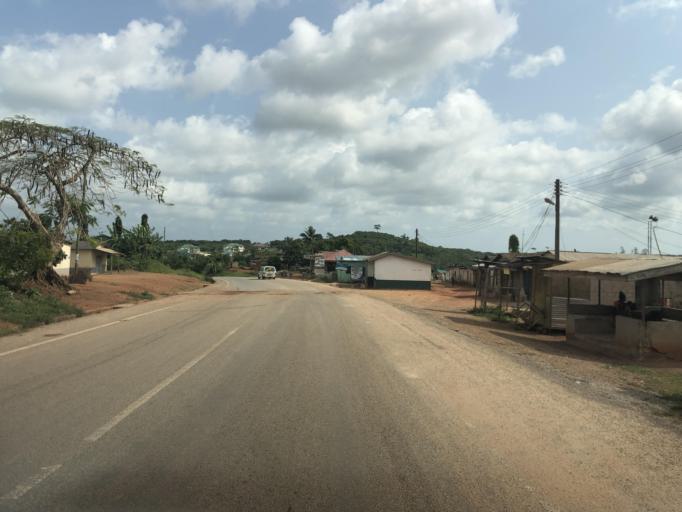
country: GH
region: Central
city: Elmina
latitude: 5.1951
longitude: -1.3197
